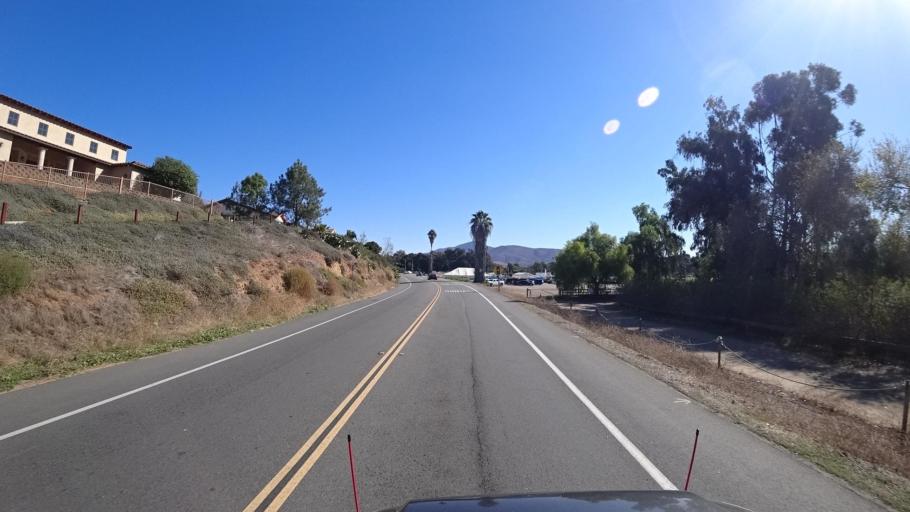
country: US
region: California
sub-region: San Diego County
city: Bonita
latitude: 32.6770
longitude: -117.0200
